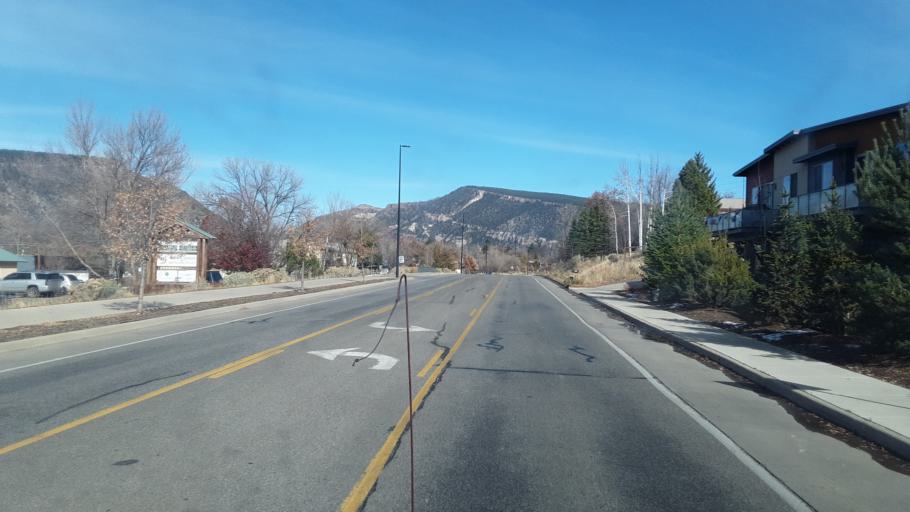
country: US
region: Colorado
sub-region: La Plata County
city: Durango
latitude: 37.2897
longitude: -107.8639
